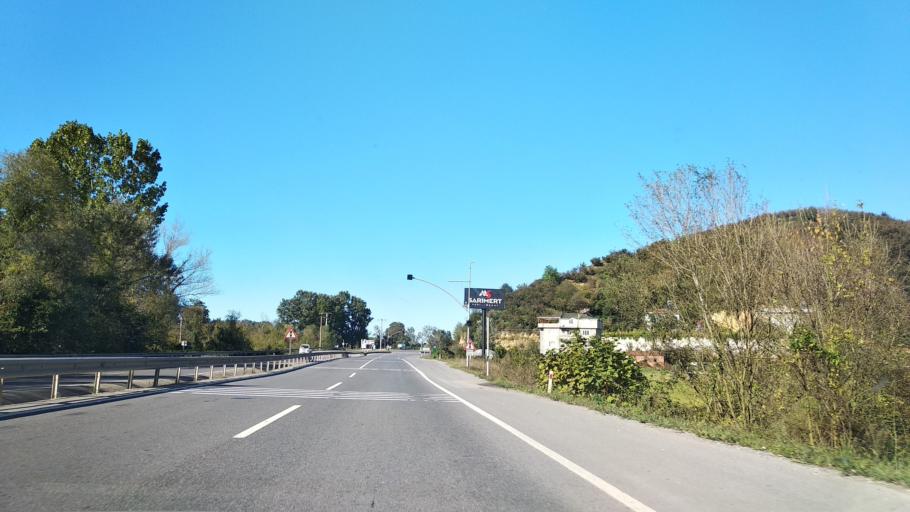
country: TR
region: Sakarya
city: Karasu
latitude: 41.0787
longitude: 30.6460
